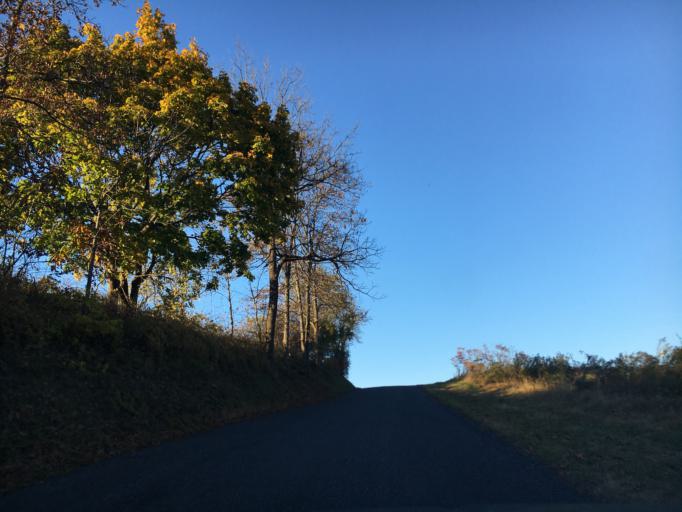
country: US
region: Pennsylvania
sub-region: Lehigh County
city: Laurys Station
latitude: 40.7085
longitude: -75.5618
